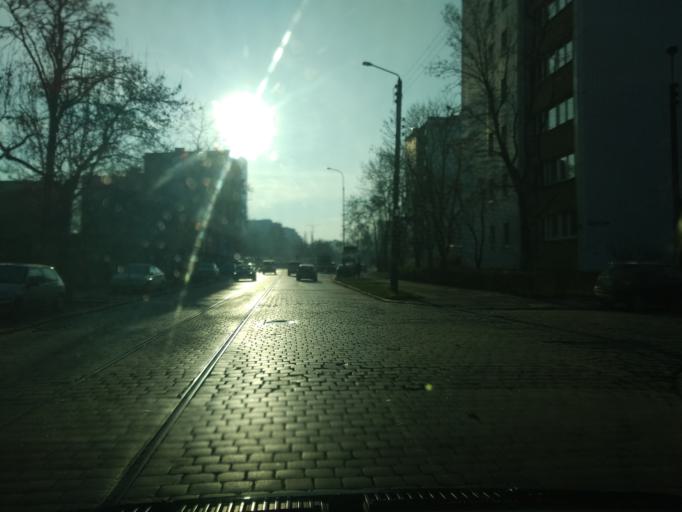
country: PL
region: Lower Silesian Voivodeship
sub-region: Powiat wroclawski
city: Wroclaw
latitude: 51.1037
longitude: 17.0125
